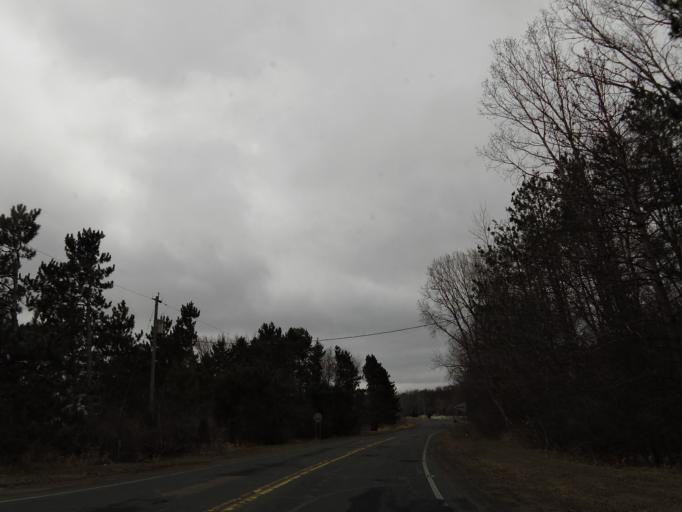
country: US
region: Minnesota
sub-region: Washington County
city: Oak Park Heights
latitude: 45.0107
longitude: -92.8310
